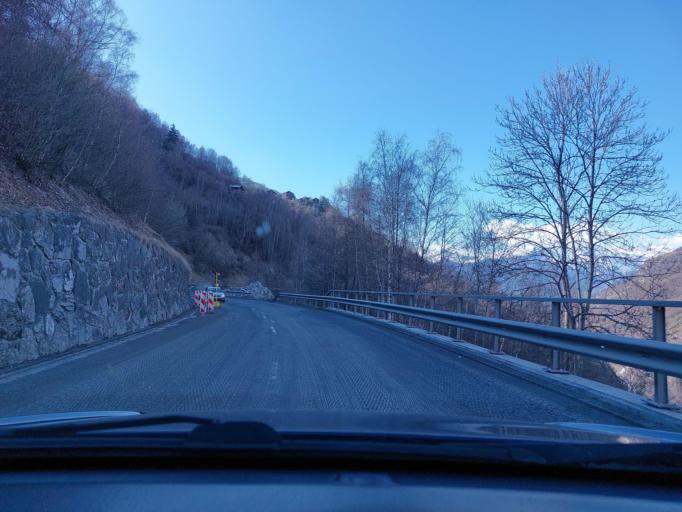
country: CH
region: Valais
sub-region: Herens District
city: Heremence
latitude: 46.1636
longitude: 7.4349
